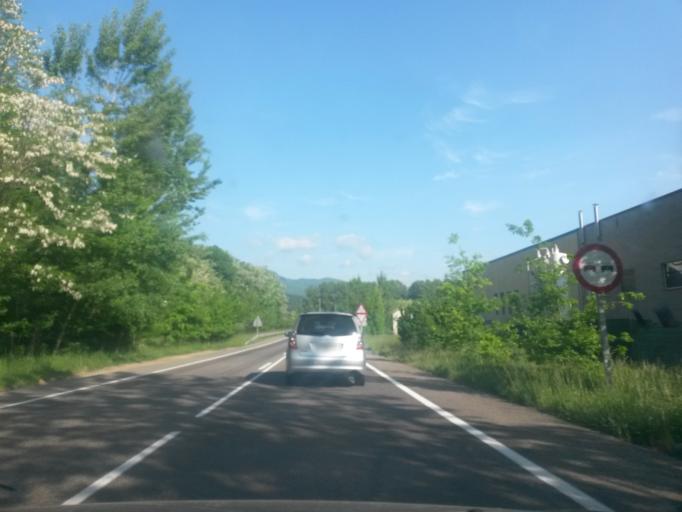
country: ES
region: Catalonia
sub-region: Provincia de Girona
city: Bas
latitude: 42.1270
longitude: 2.4512
